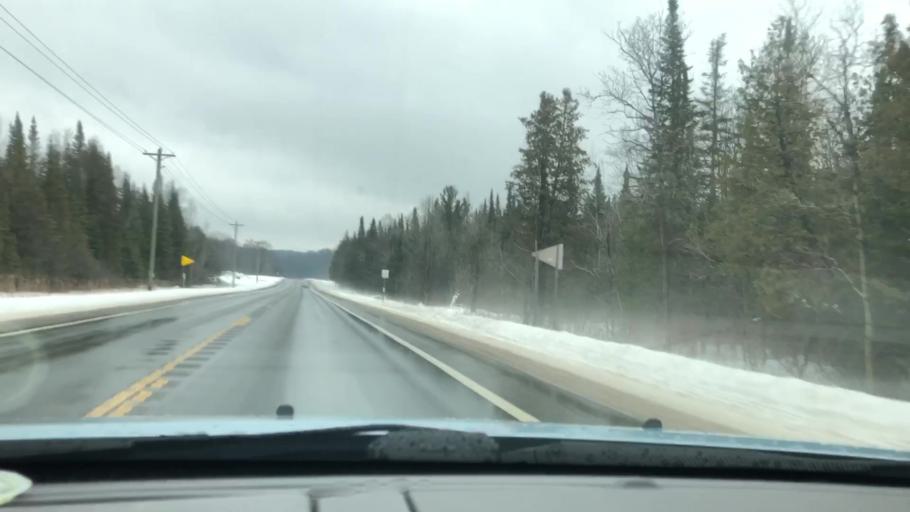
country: US
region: Michigan
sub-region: Charlevoix County
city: Boyne City
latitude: 45.0908
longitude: -84.9460
